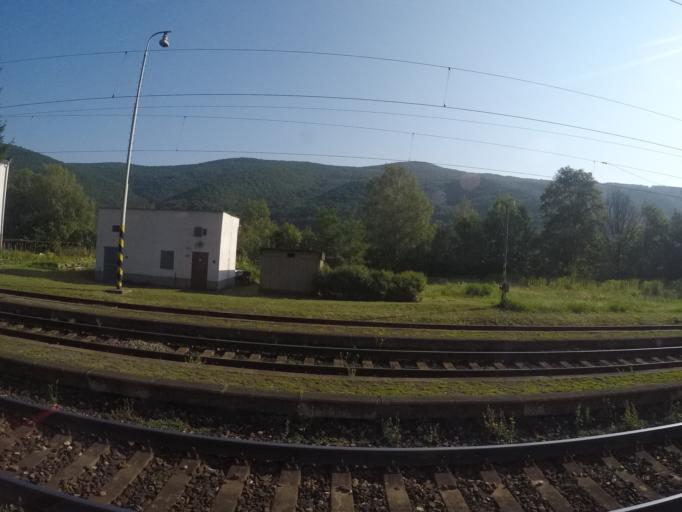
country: SK
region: Presovsky
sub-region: Okres Presov
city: Presov
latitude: 48.8737
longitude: 21.1349
